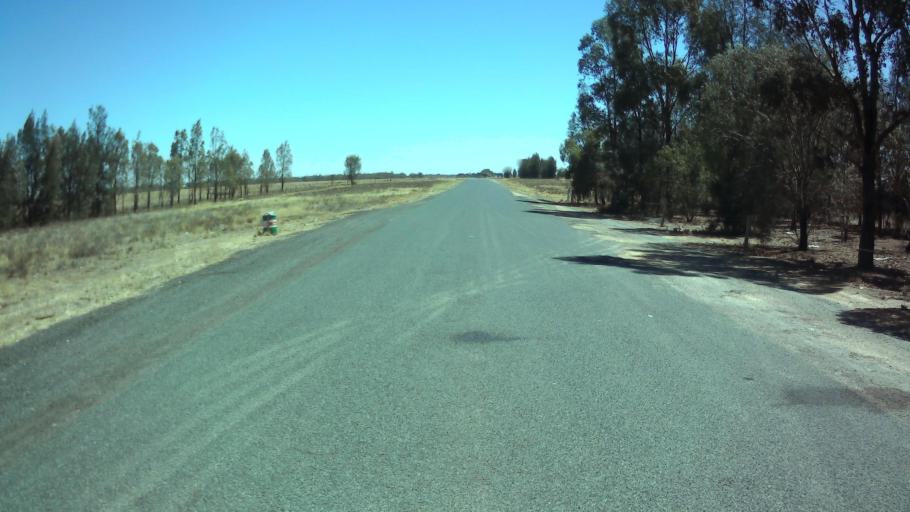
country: AU
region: New South Wales
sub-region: Bland
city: West Wyalong
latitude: -33.7549
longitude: 147.5272
